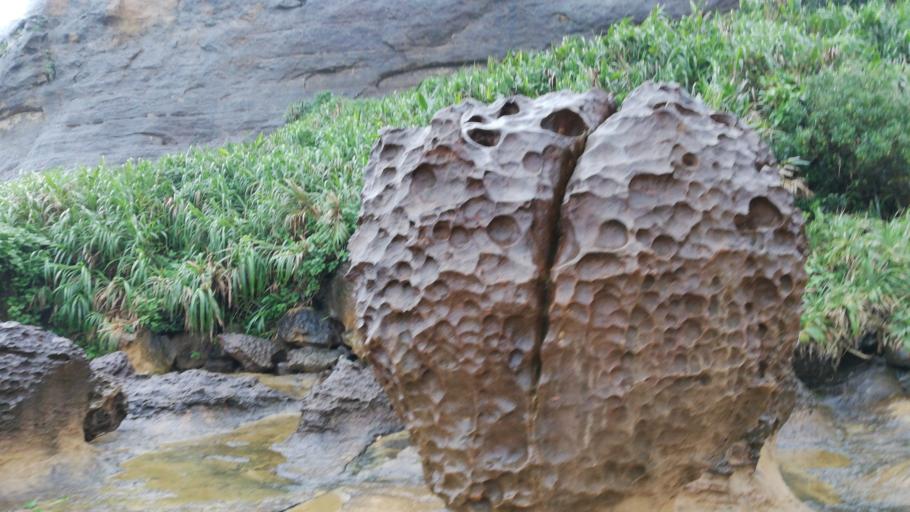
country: TW
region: Taiwan
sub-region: Keelung
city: Keelung
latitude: 25.2077
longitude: 121.6915
